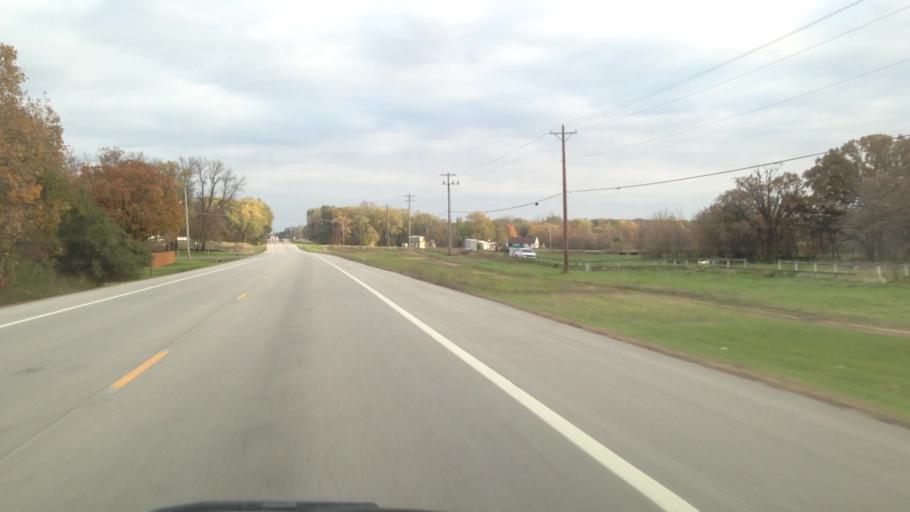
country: US
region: Minnesota
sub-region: Olmsted County
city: Rochester
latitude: 43.9816
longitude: -92.4002
